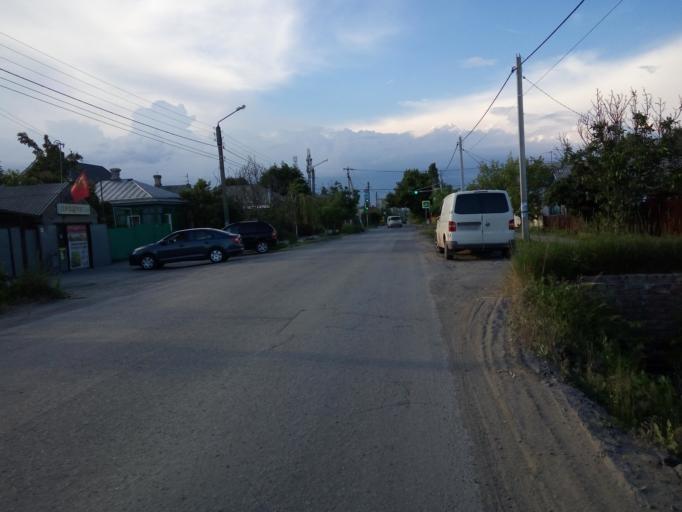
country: RU
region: Rostov
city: Bataysk
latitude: 47.1173
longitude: 39.7396
